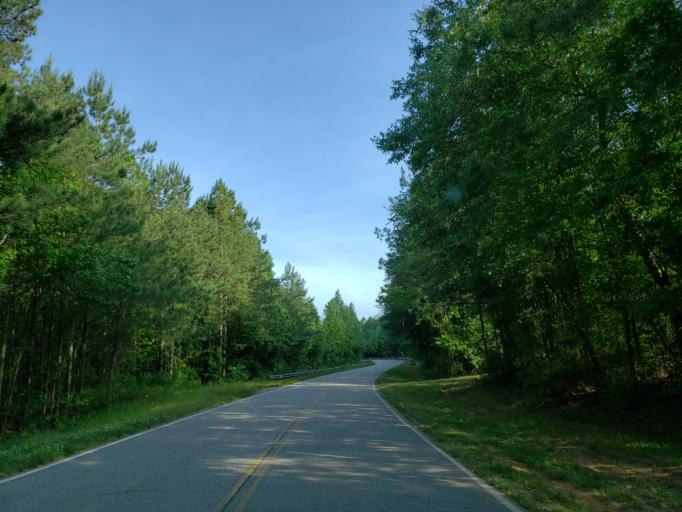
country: US
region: Georgia
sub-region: Carroll County
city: Bowdon
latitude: 33.4906
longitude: -85.3056
